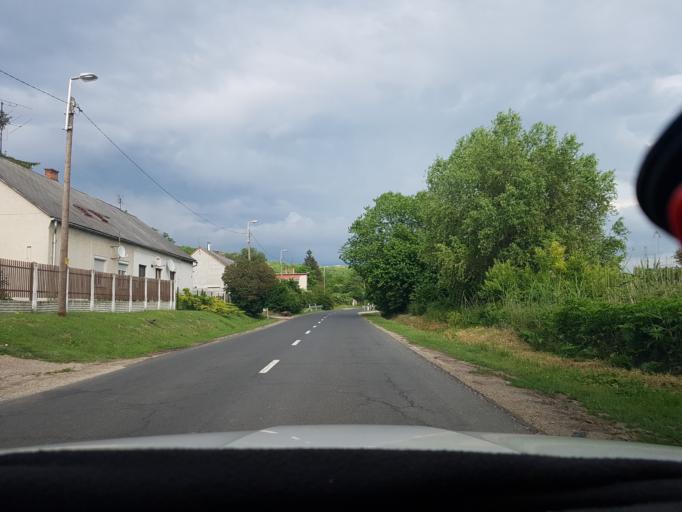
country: HU
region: Komarom-Esztergom
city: Tokod
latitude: 47.7038
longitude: 18.6472
